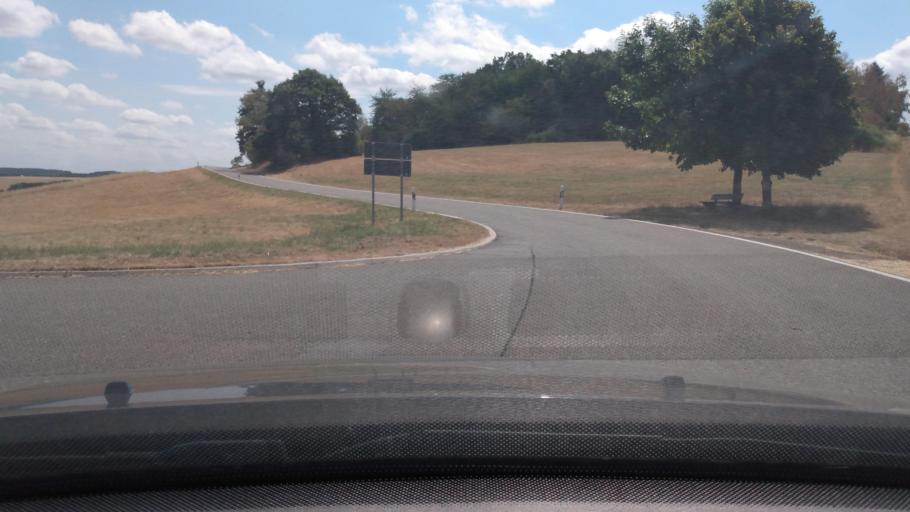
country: DE
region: Rheinland-Pfalz
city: Kommen
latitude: 49.8949
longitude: 7.1551
